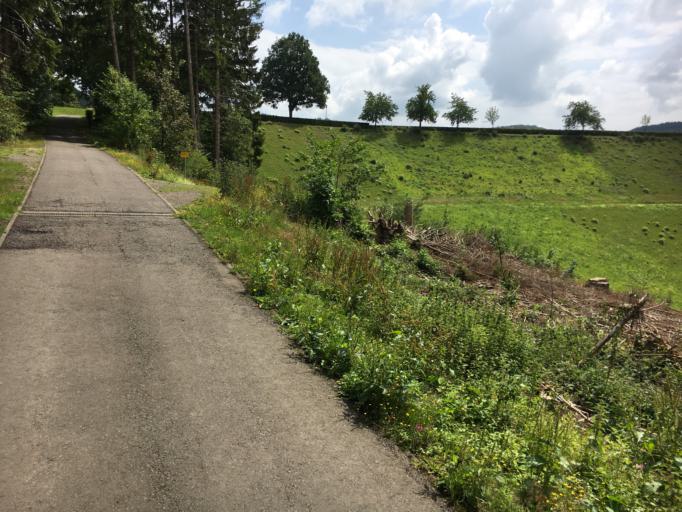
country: DE
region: North Rhine-Westphalia
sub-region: Regierungsbezirk Arnsberg
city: Attendorn
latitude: 51.1139
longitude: 7.8889
